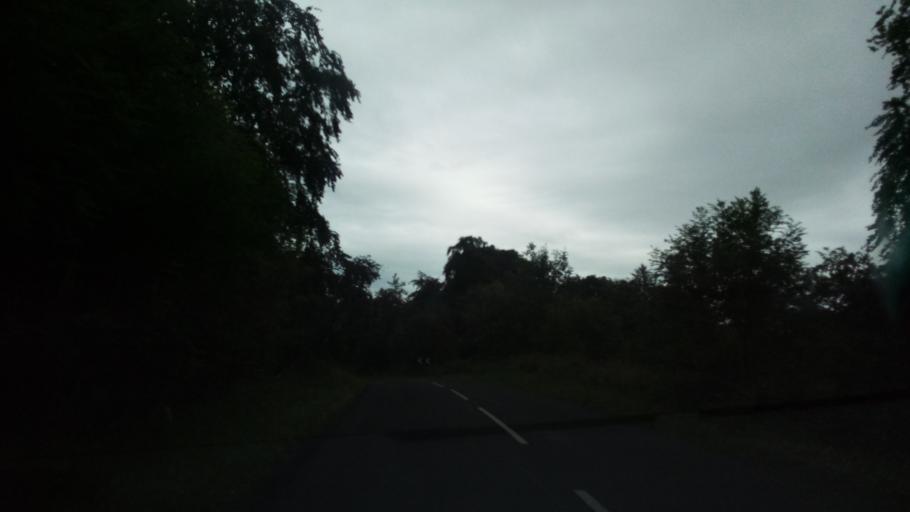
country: GB
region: England
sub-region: County Durham
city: Holwick
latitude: 54.5908
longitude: -2.1577
